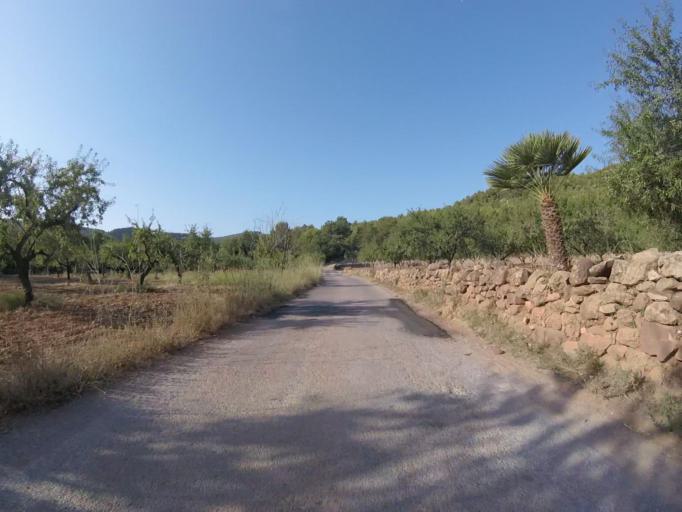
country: ES
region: Valencia
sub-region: Provincia de Castello
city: Cabanes
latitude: 40.1094
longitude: 0.0639
